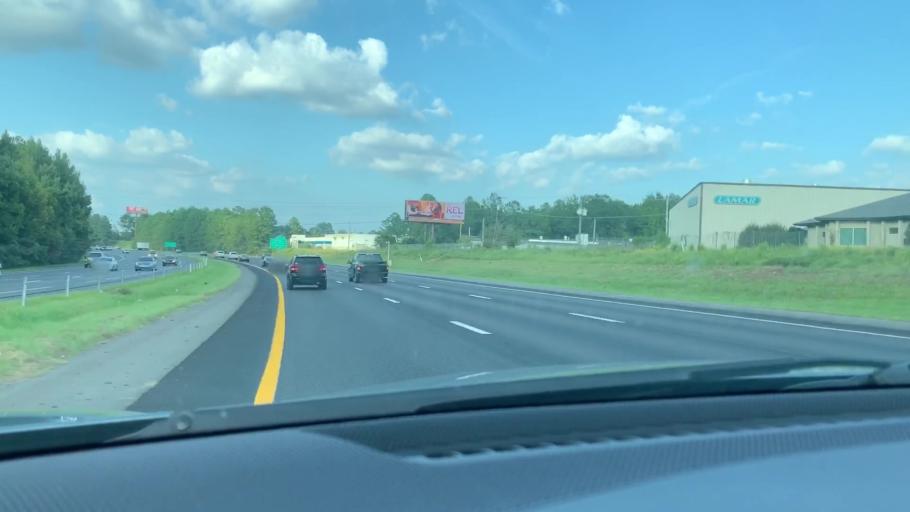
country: US
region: South Carolina
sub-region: Richland County
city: Forest Acres
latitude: 33.9580
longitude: -80.9542
